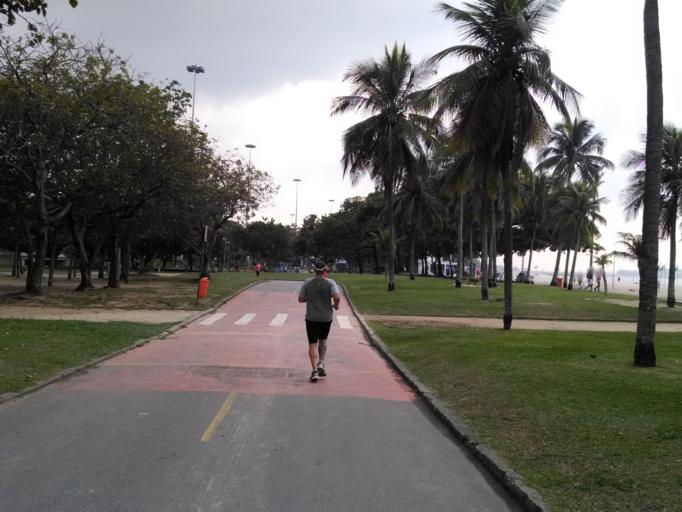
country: BR
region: Rio de Janeiro
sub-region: Rio De Janeiro
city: Rio de Janeiro
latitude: -22.9313
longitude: -43.1723
